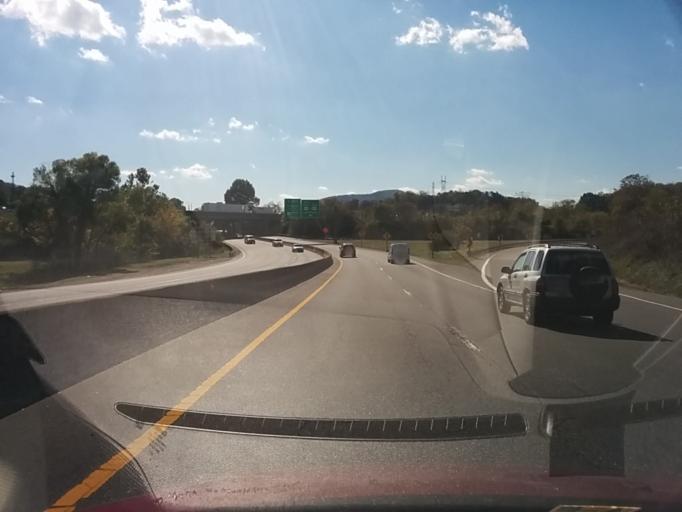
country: US
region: Virginia
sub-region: Botetourt County
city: Daleville
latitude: 37.3904
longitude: -79.9058
